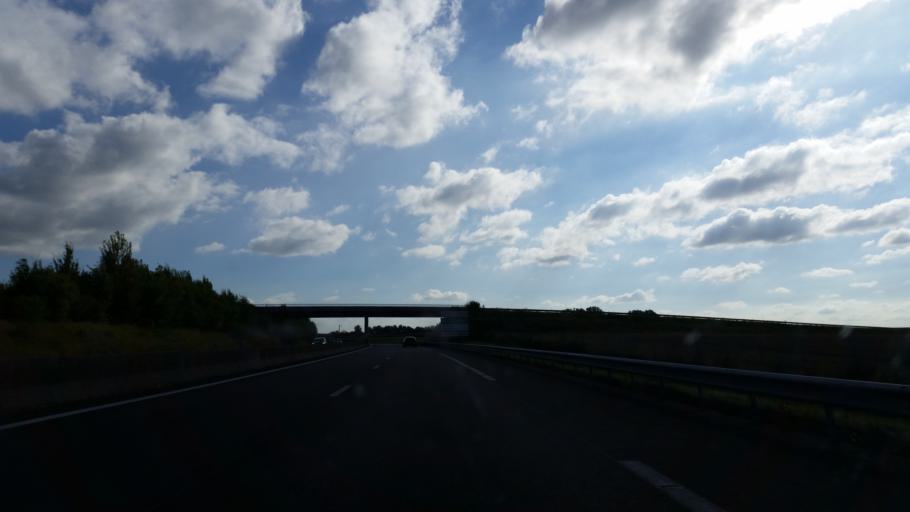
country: FR
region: Haute-Normandie
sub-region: Departement de la Seine-Maritime
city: Aumale
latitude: 49.7748
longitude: 1.7186
